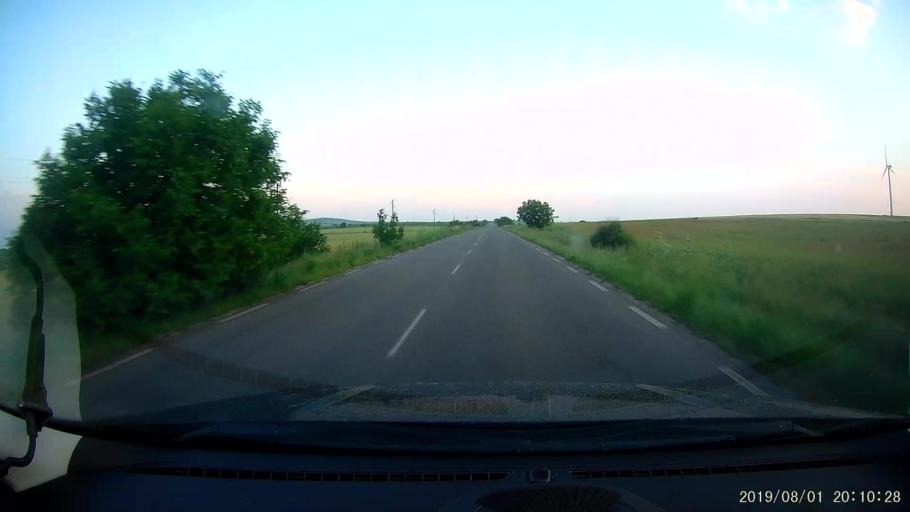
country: BG
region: Yambol
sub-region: Obshtina Yambol
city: Yambol
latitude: 42.4809
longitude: 26.5995
